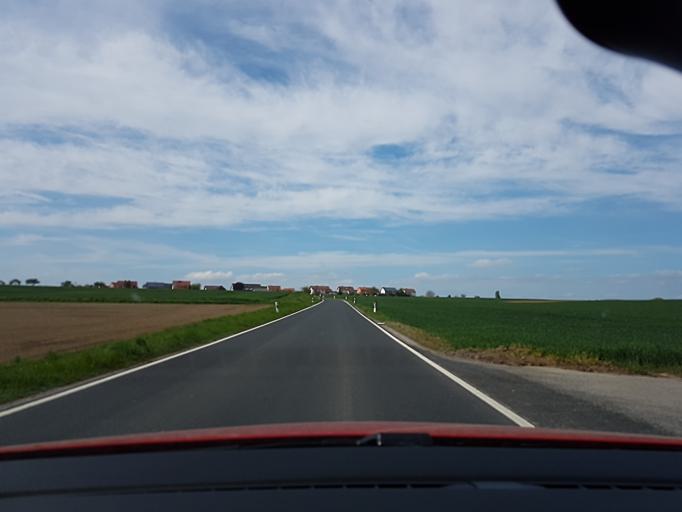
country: DE
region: Bavaria
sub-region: Regierungsbezirk Unterfranken
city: Unterpleichfeld
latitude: 49.9028
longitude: 10.0196
